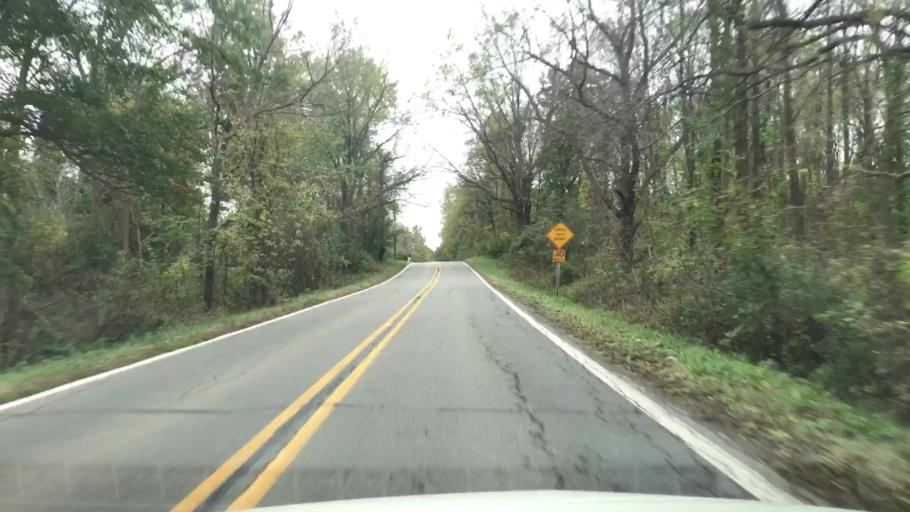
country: US
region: Michigan
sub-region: Macomb County
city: Shelby
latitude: 42.7358
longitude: -83.0567
